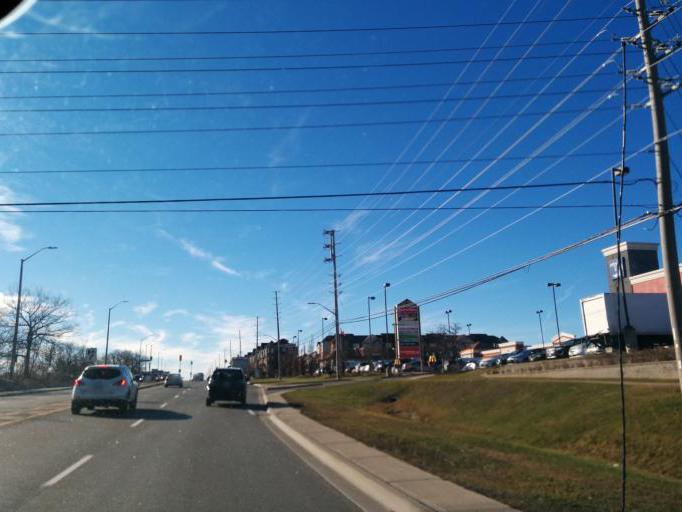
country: CA
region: Ontario
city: Mississauga
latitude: 43.5718
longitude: -79.6264
